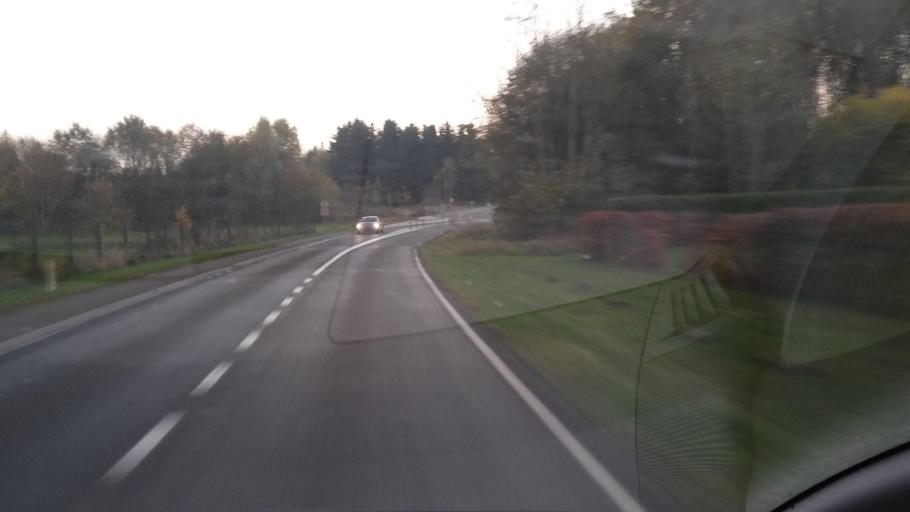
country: BE
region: Wallonia
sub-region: Province du Luxembourg
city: Etalle
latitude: 49.6651
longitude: 5.5973
